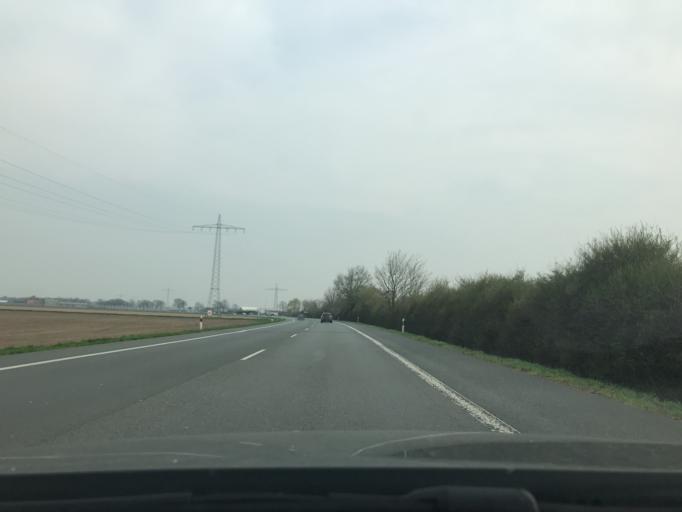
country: DE
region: North Rhine-Westphalia
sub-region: Regierungsbezirk Dusseldorf
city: Wachtendonk
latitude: 51.4541
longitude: 6.3853
